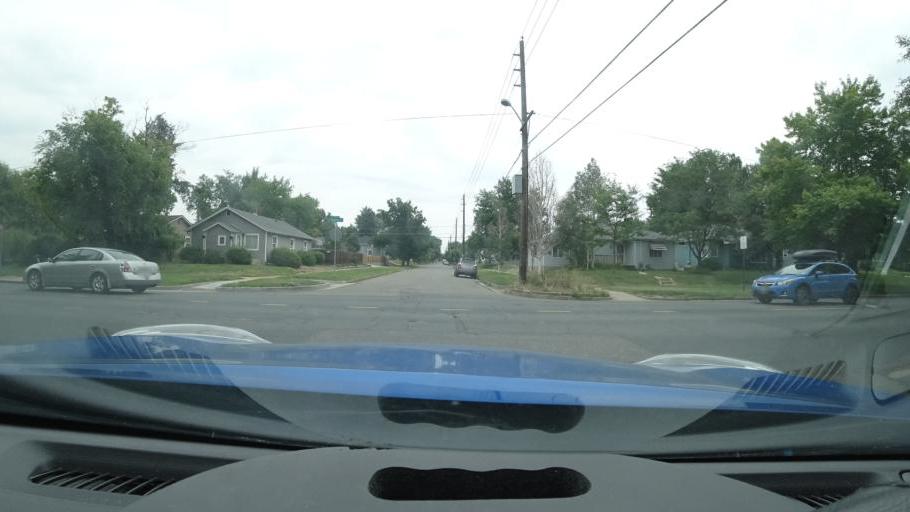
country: US
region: Colorado
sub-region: Arapahoe County
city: Englewood
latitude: 39.6840
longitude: -104.9735
